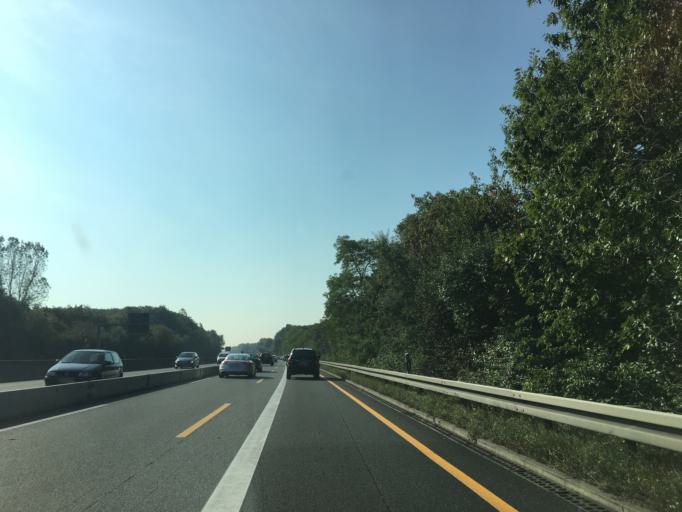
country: DE
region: Hesse
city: Lorsch
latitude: 49.6519
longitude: 8.5519
